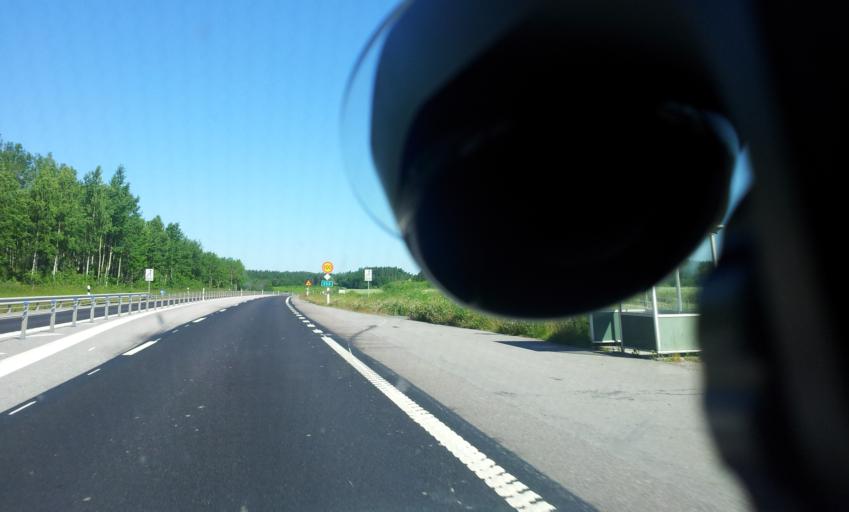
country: SE
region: OEstergoetland
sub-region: Soderkopings Kommun
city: Soederkoeping
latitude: 58.5091
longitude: 16.2922
